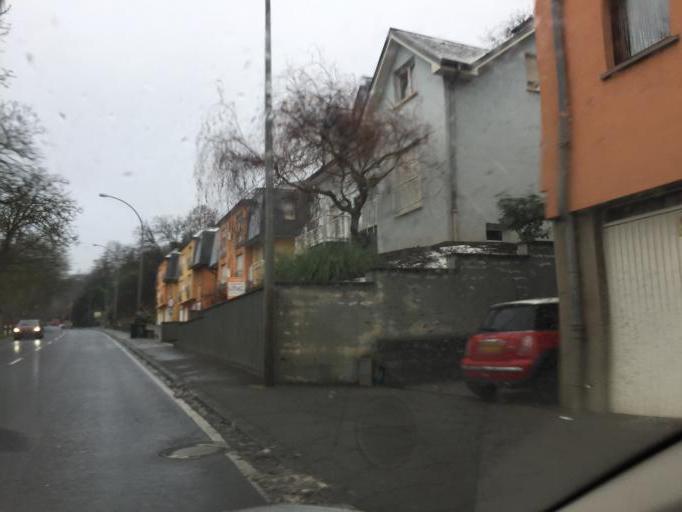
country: LU
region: Diekirch
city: Warken
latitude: 49.8480
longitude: 6.0892
